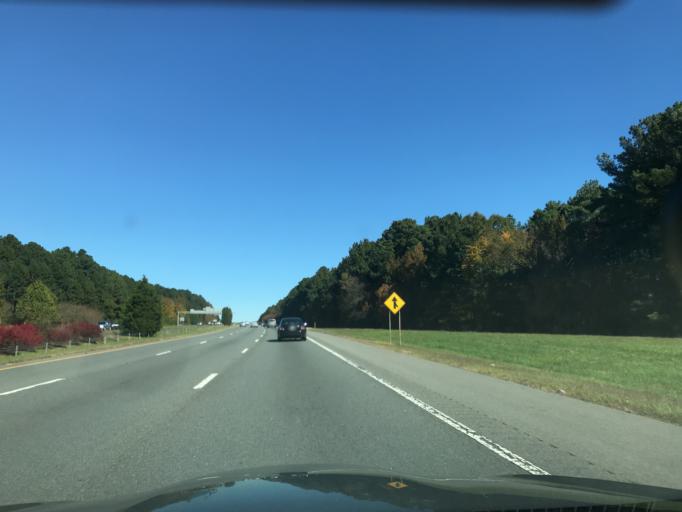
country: US
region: North Carolina
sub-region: Durham County
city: Durham
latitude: 35.9126
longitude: -78.8644
